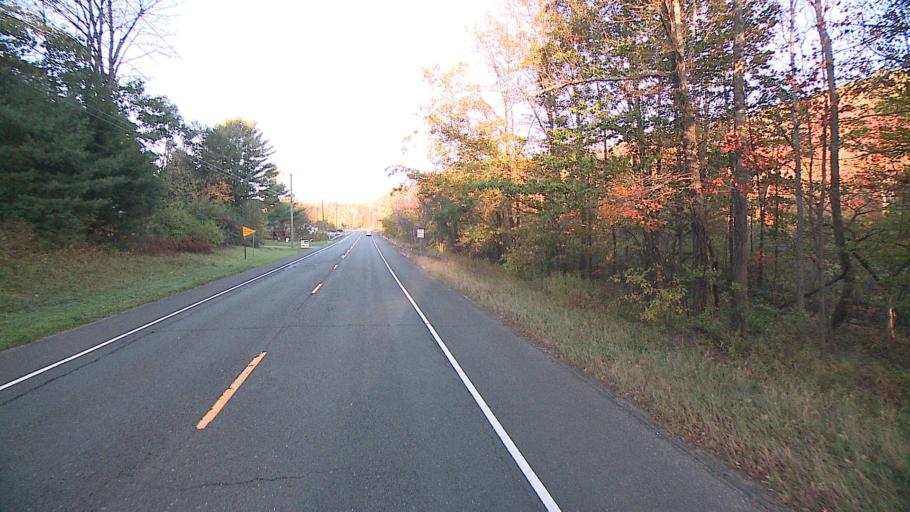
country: US
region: Connecticut
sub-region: Litchfield County
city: Winsted
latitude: 41.9124
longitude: -73.0292
